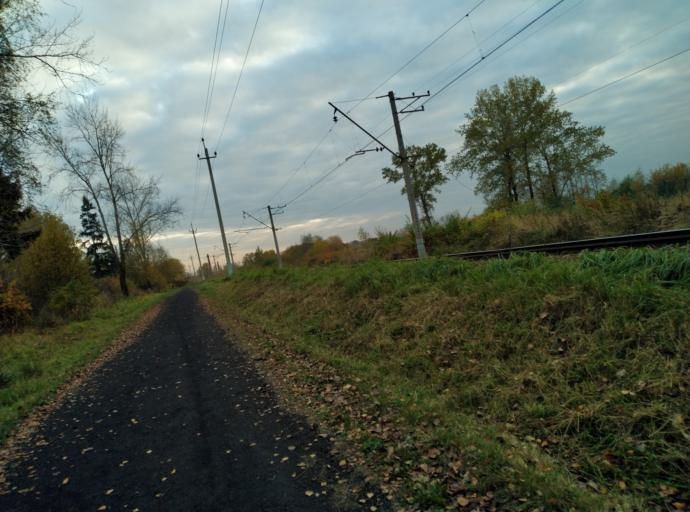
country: RU
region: Moskovskaya
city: Bol'shiye Vyazemy
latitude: 55.6245
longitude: 36.9753
